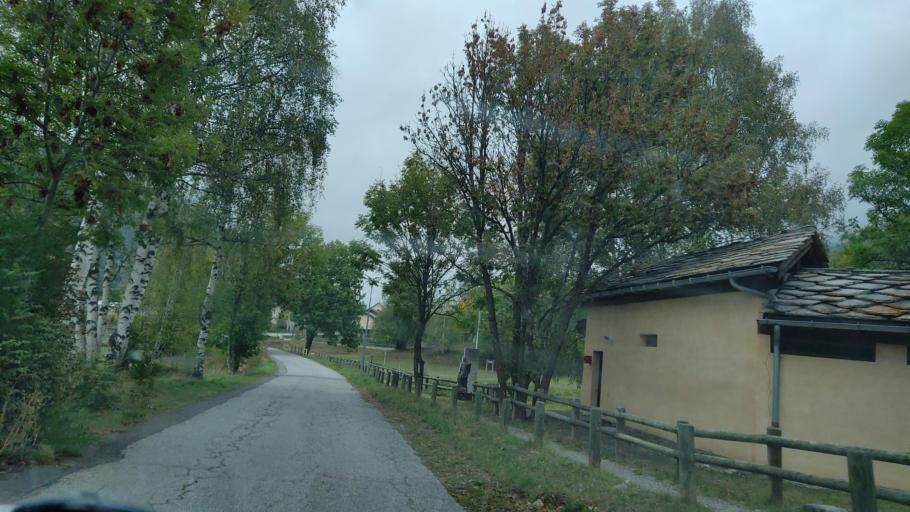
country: FR
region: Rhone-Alpes
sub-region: Departement de la Savoie
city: Modane
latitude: 45.2267
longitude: 6.7791
